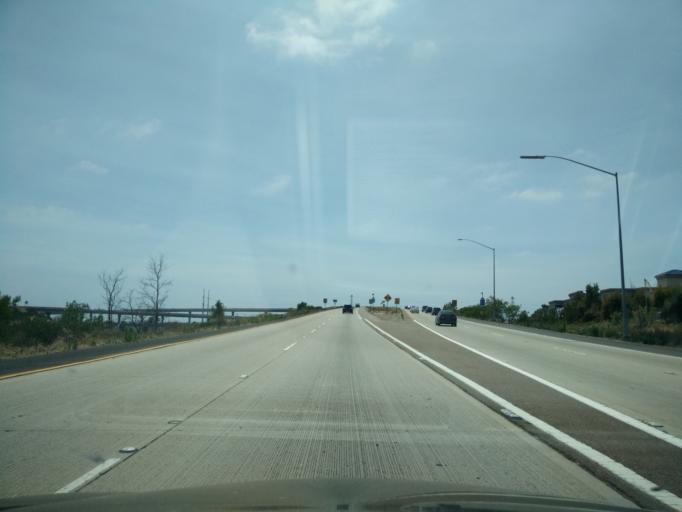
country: US
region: California
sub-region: San Diego County
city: Chula Vista
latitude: 32.6532
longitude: -117.0986
